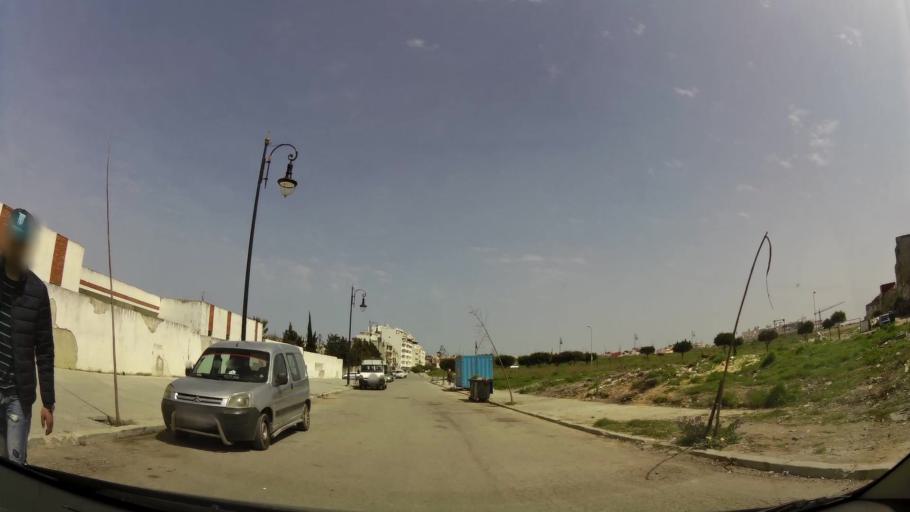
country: MA
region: Tanger-Tetouan
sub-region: Tanger-Assilah
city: Tangier
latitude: 35.7552
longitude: -5.8460
